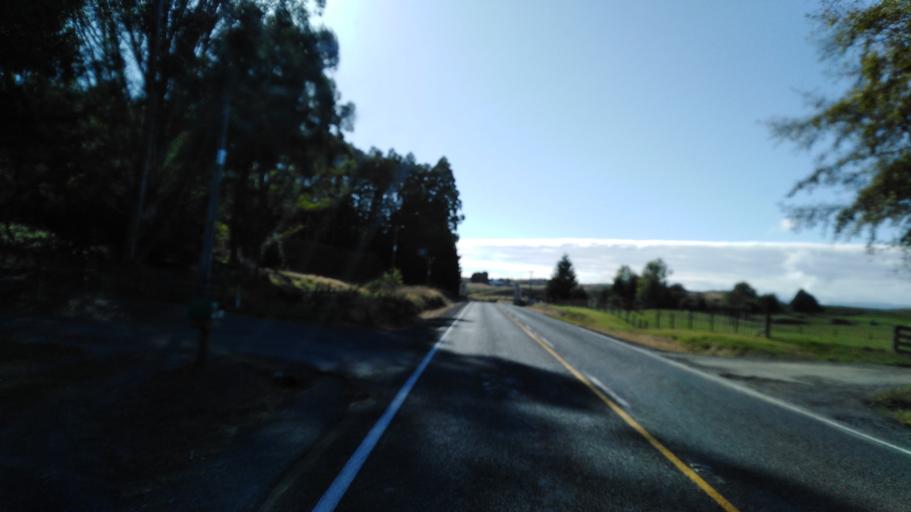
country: NZ
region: Waikato
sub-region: Taupo District
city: Taupo
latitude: -38.5966
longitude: 176.1317
